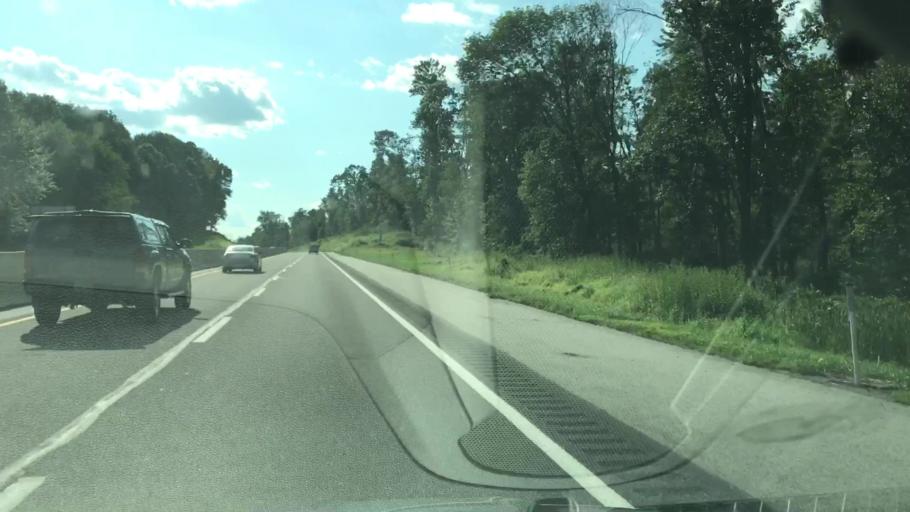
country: US
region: Pennsylvania
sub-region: Lebanon County
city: Cornwall
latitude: 40.2284
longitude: -76.4591
